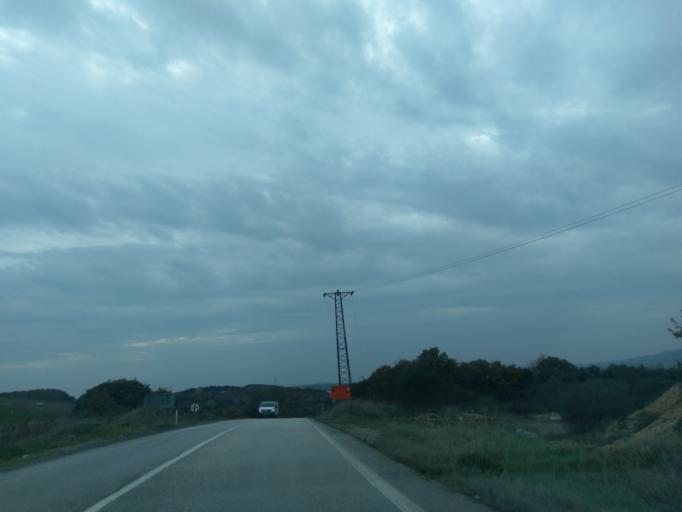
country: TR
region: Istanbul
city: Canta
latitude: 41.1598
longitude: 28.1067
